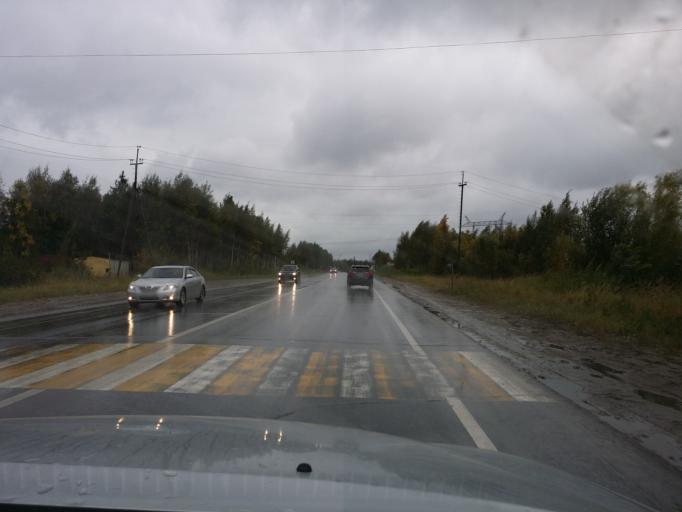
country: RU
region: Khanty-Mansiyskiy Avtonomnyy Okrug
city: Megion
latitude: 61.0543
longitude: 76.1130
